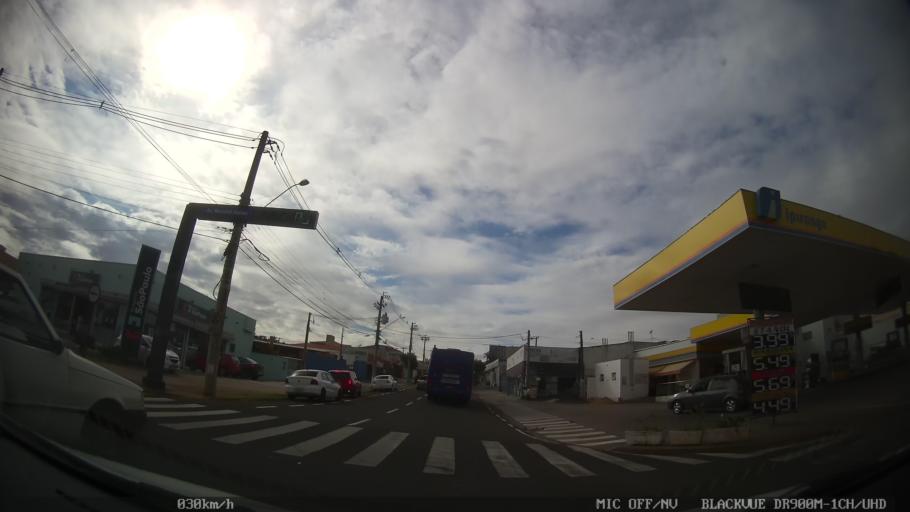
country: BR
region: Sao Paulo
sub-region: Sao Jose Do Rio Preto
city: Sao Jose do Rio Preto
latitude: -20.8165
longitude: -49.3656
